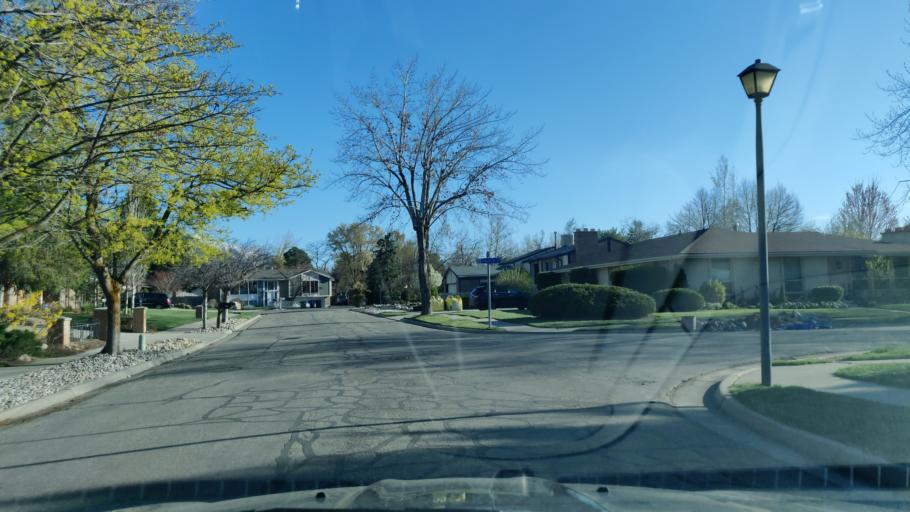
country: US
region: Utah
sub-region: Salt Lake County
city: Cottonwood Heights
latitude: 40.6176
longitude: -111.8174
